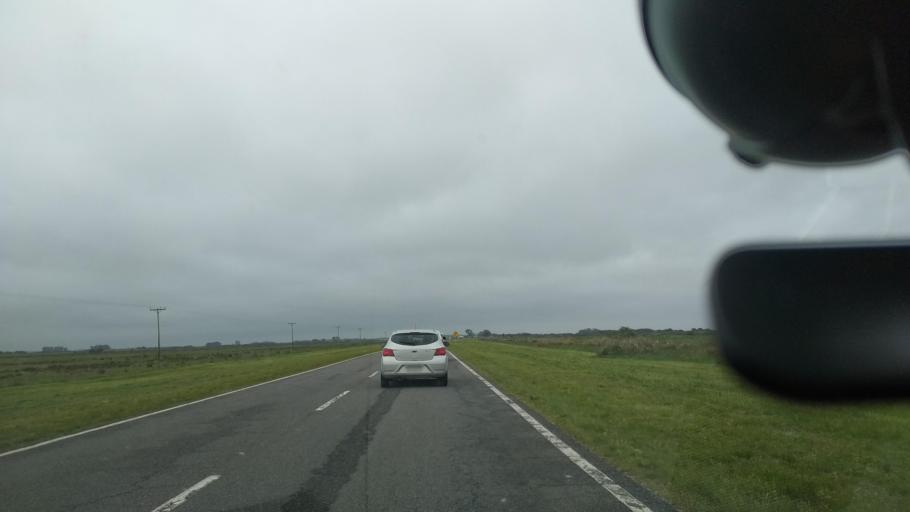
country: AR
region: Buenos Aires
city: Veronica
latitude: -35.6055
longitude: -57.2804
